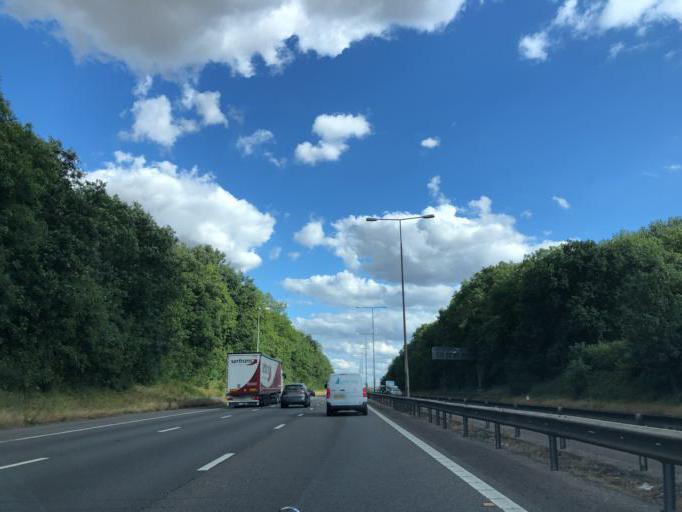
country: GB
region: England
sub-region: Northamptonshire
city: Hartwell
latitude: 52.1571
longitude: -0.8500
